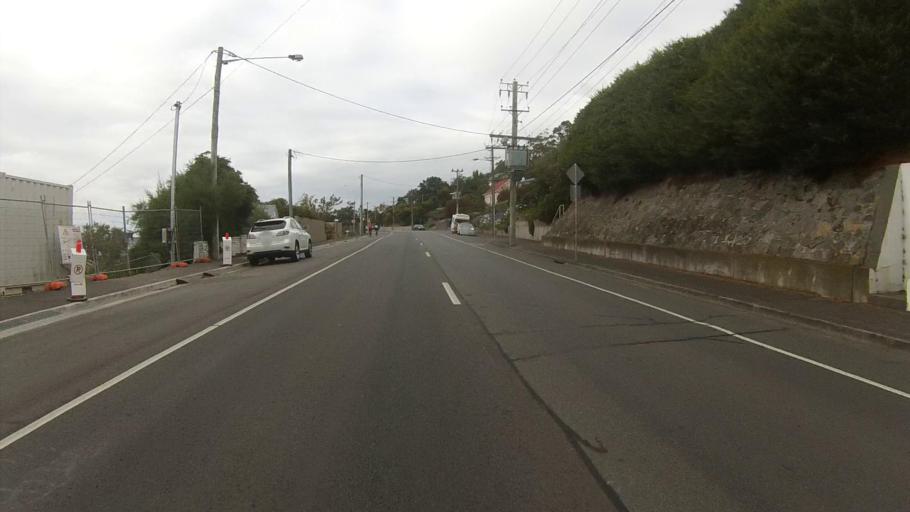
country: AU
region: Tasmania
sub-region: Kingborough
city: Taroona
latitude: -42.9202
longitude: 147.3600
